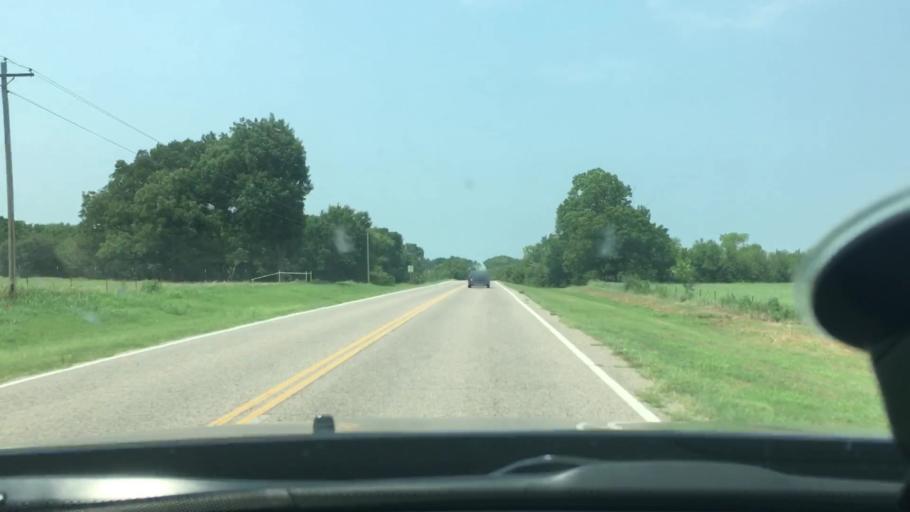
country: US
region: Texas
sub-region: Grayson County
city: Sherwood Shores
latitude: 33.9840
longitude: -96.9308
